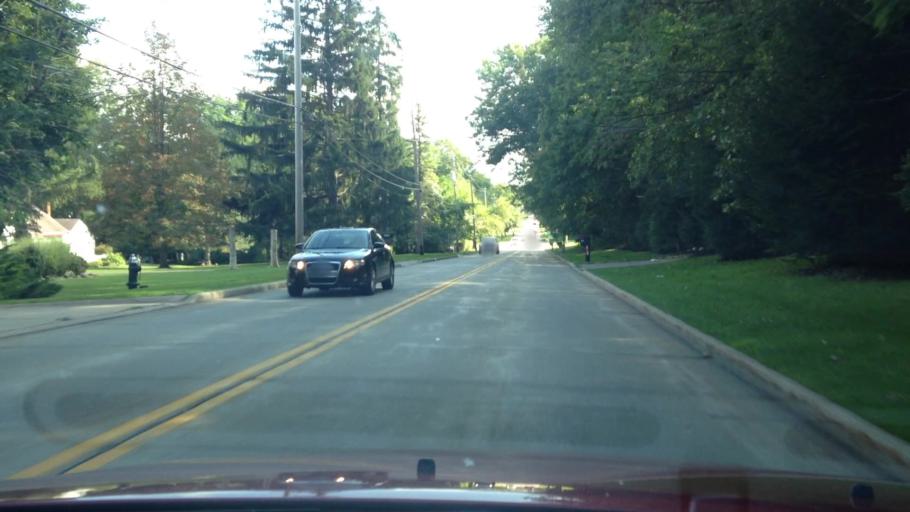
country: US
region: Ohio
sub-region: Cuyahoga County
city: Orange
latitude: 41.4522
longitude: -81.4635
